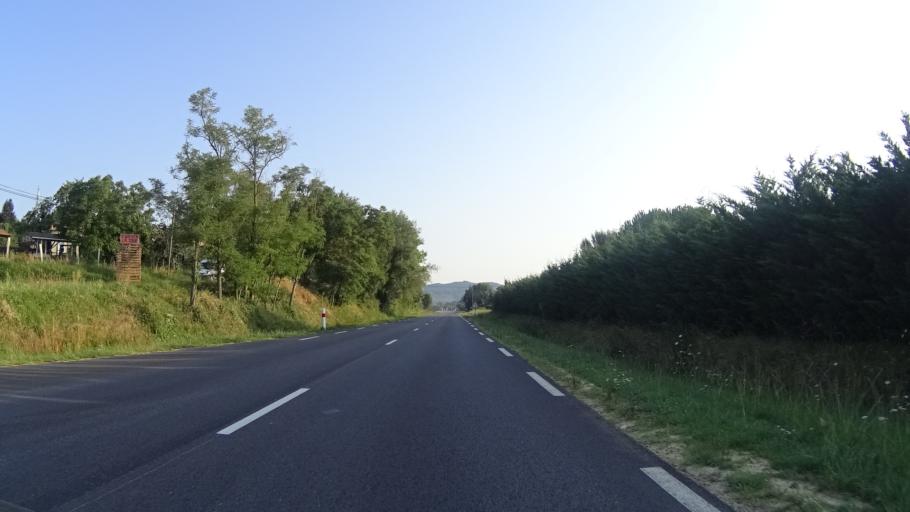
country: FR
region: Midi-Pyrenees
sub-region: Departement de l'Ariege
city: Mirepoix
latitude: 43.0323
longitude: 1.8970
